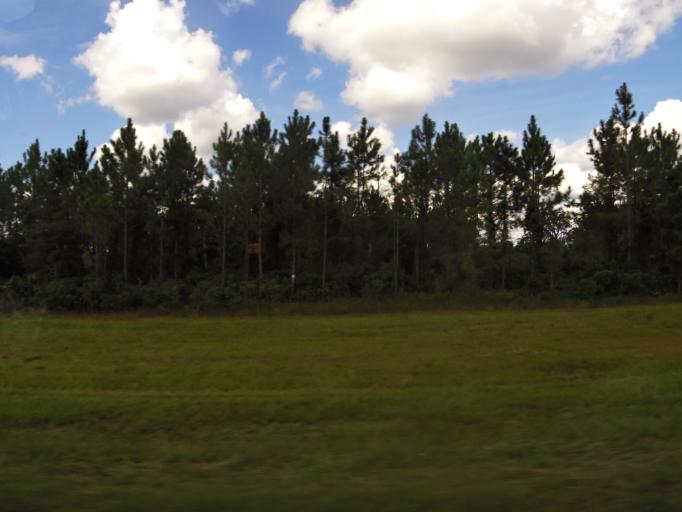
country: US
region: Florida
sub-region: Hamilton County
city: Jasper
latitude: 30.6779
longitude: -82.7077
